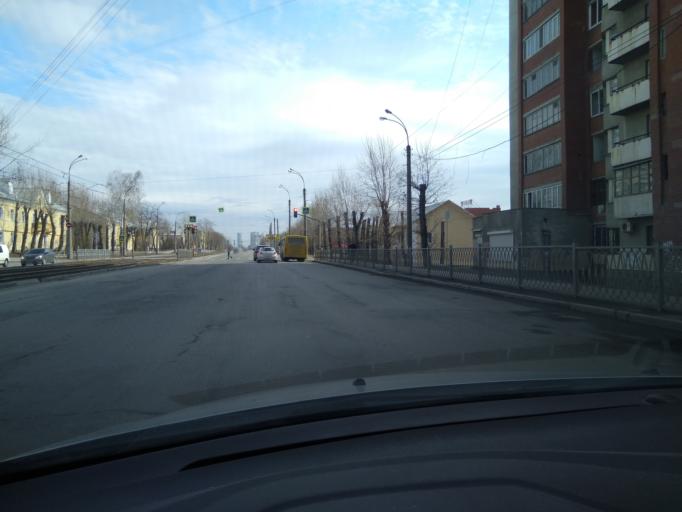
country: RU
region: Sverdlovsk
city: Shuvakish
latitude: 56.8705
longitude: 60.5218
